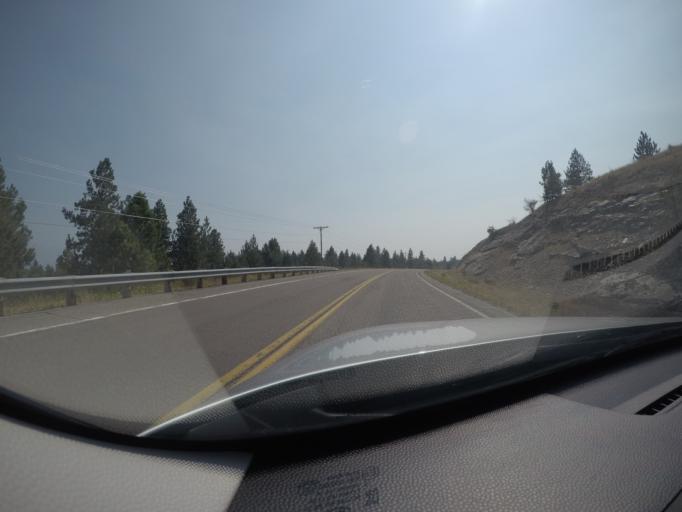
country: US
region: Montana
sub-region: Lake County
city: Polson
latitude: 47.7519
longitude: -114.1686
